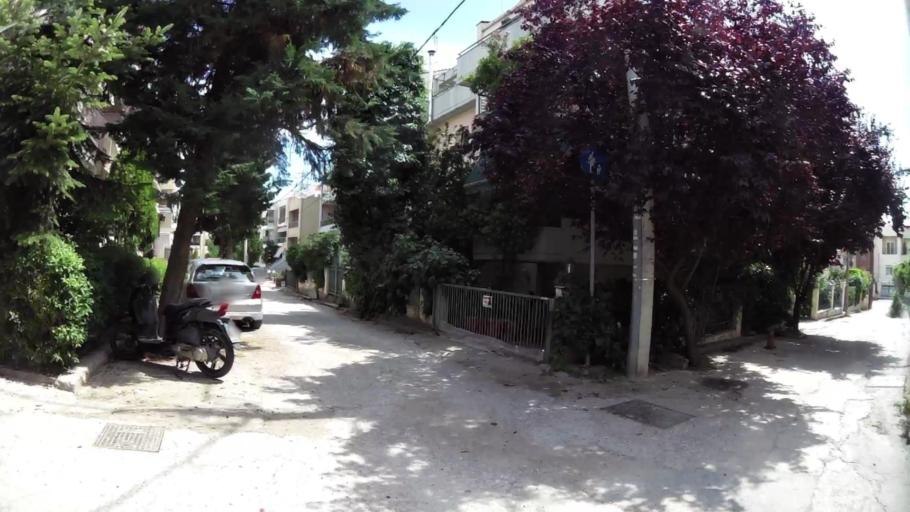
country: GR
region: Central Macedonia
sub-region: Nomos Thessalonikis
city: Pylaia
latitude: 40.5949
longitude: 22.9780
